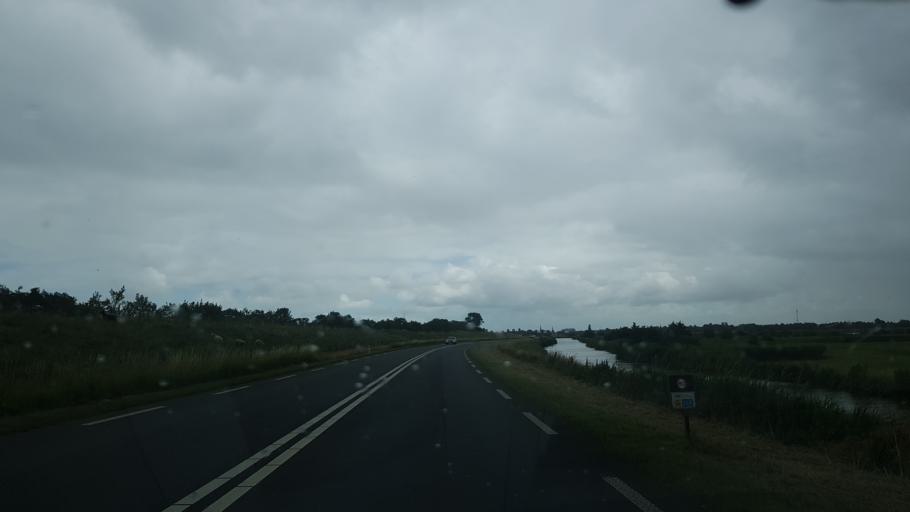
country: NL
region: North Holland
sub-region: Gemeente Medemblik
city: Opperdoes
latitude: 52.7536
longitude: 5.0481
